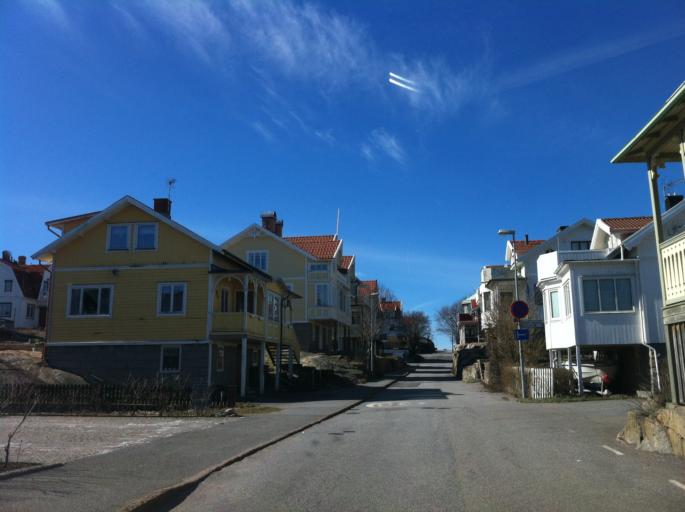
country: SE
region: Vaestra Goetaland
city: Smoegen
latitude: 58.3544
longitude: 11.2249
